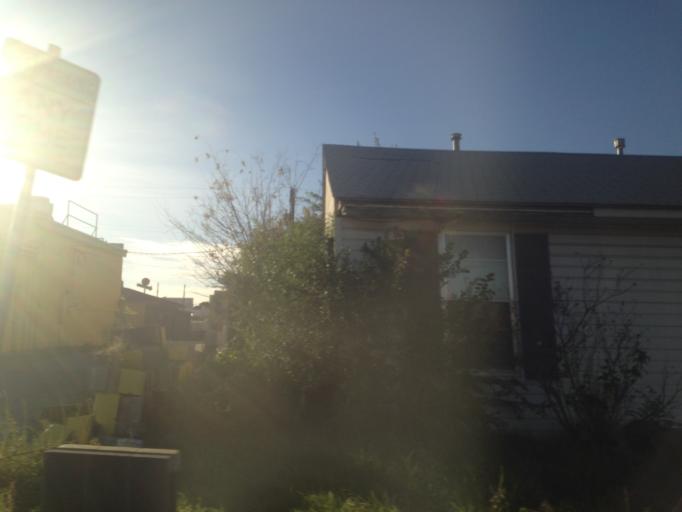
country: US
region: Texas
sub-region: Taylor County
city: Abilene
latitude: 32.4329
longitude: -99.7596
